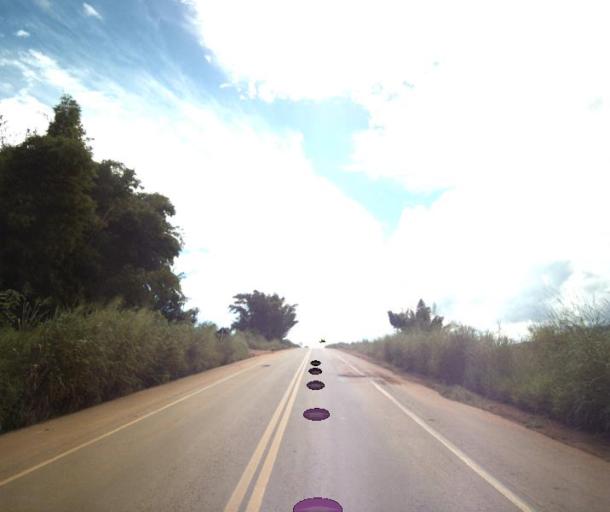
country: BR
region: Goias
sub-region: Pirenopolis
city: Pirenopolis
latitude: -16.0118
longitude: -49.1215
